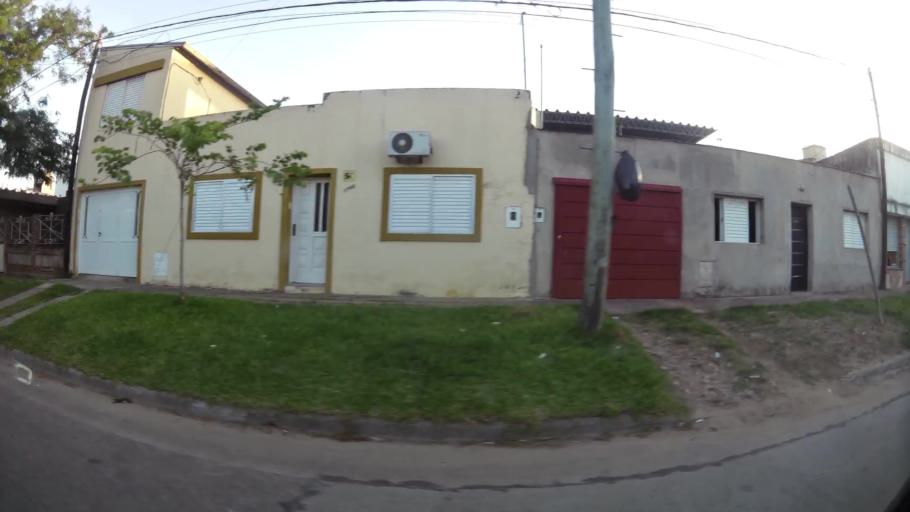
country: AR
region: Santa Fe
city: Santa Fe de la Vera Cruz
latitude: -31.6039
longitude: -60.6842
